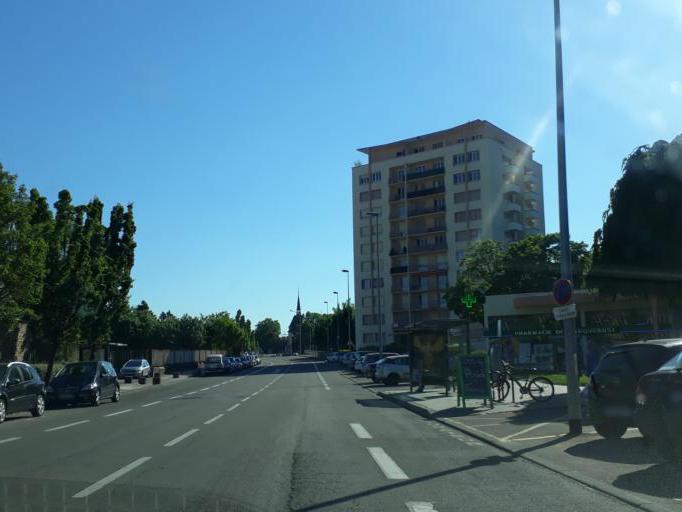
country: FR
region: Bourgogne
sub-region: Departement de la Cote-d'Or
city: Dijon
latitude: 47.3182
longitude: 5.0275
